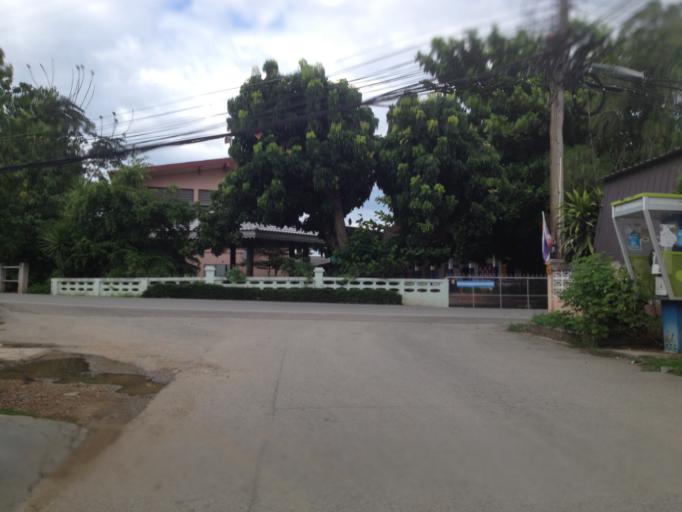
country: TH
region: Chiang Mai
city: Hang Dong
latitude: 18.6991
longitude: 98.9126
